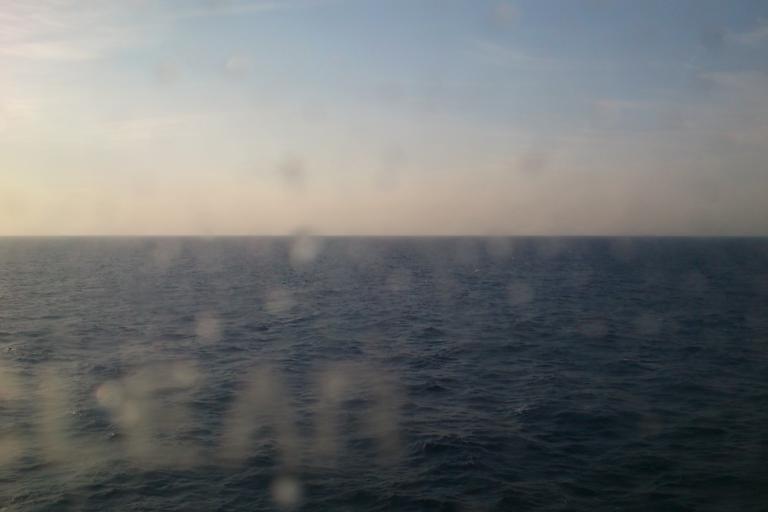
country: JP
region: Ishikawa
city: Nanao
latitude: 37.7411
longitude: 136.4018
